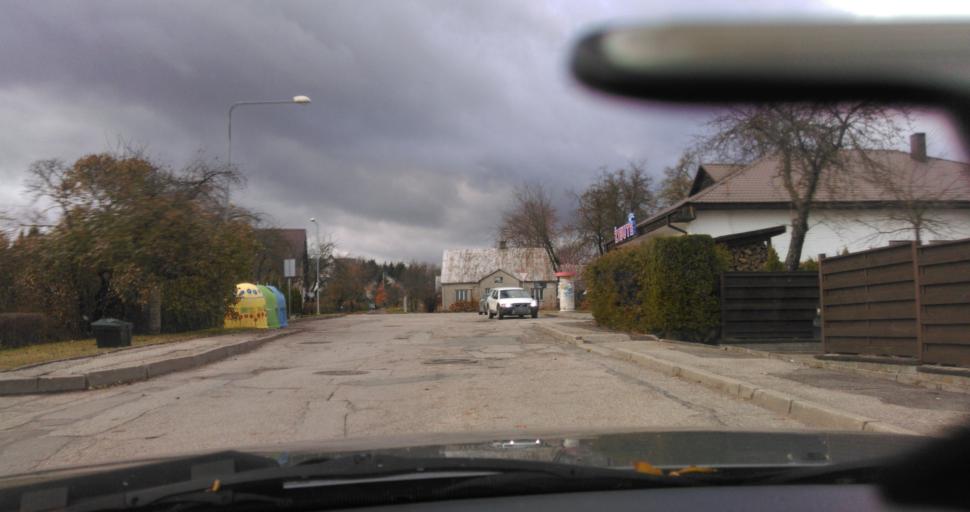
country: LT
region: Utenos apskritis
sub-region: Utena
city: Utena
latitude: 55.4916
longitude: 25.6002
